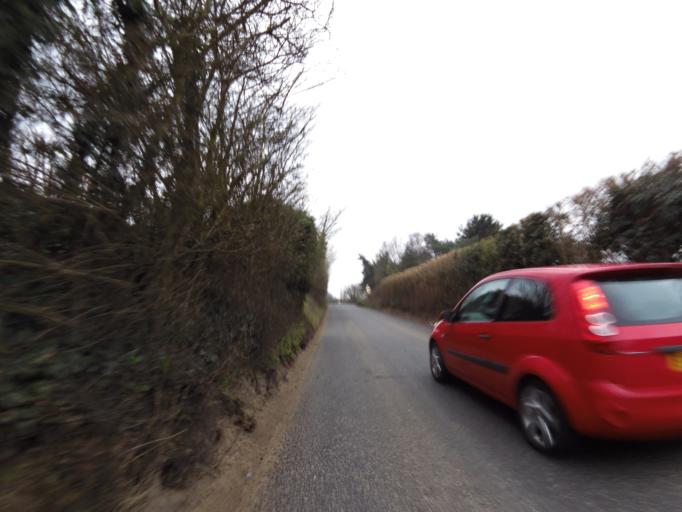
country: GB
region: England
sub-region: Suffolk
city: Wickham Market
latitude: 52.1558
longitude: 1.3881
